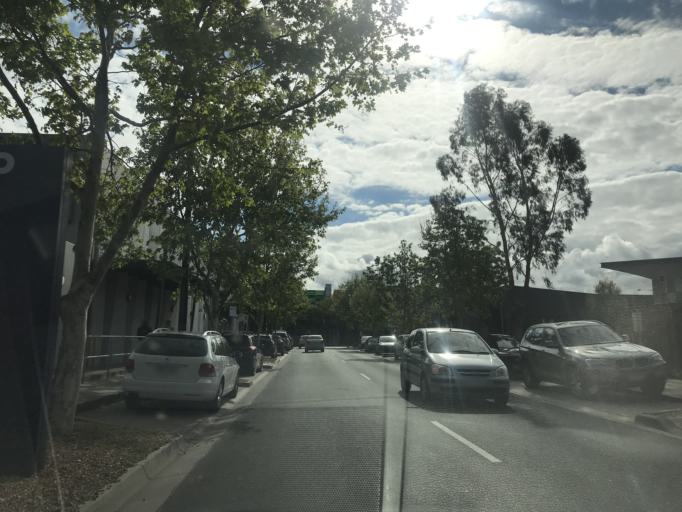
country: AU
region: Victoria
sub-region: Wyndham
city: Williams Landing
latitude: -37.8825
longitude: 144.7367
